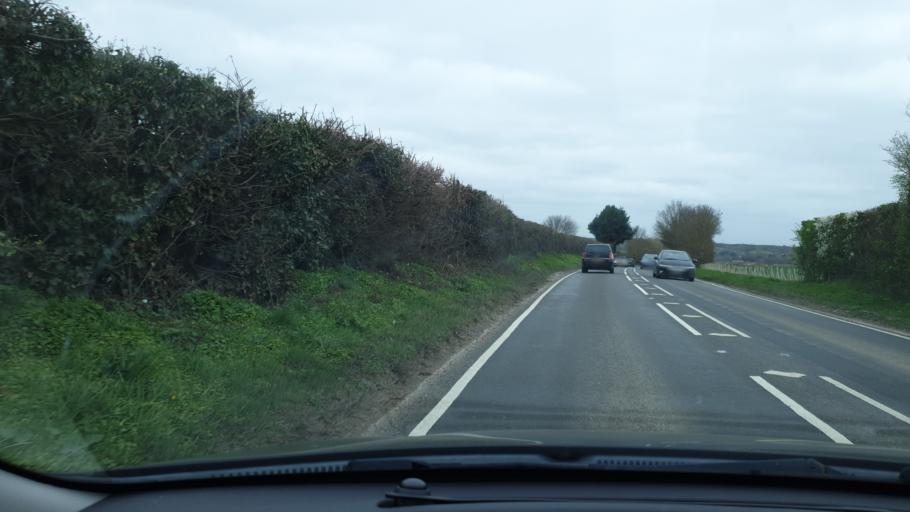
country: GB
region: England
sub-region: Essex
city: Great Horkesley
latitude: 51.9579
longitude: 0.8702
